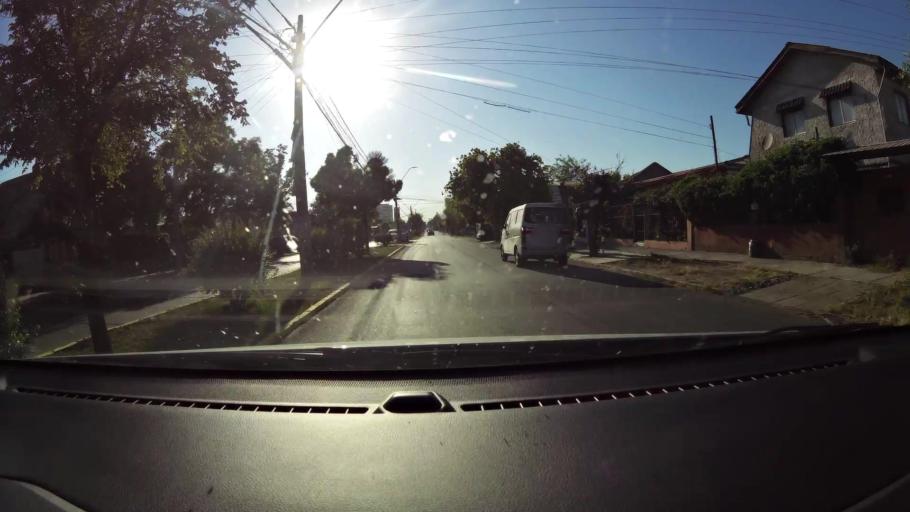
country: CL
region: Santiago Metropolitan
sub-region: Provincia de Maipo
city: San Bernardo
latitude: -33.5362
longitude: -70.6783
